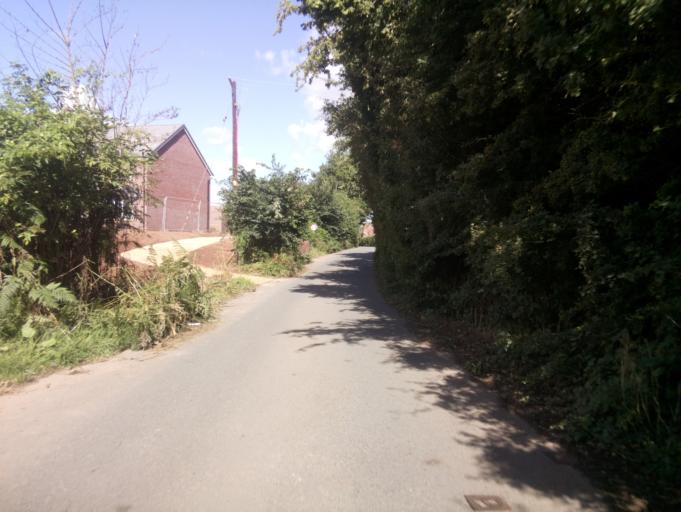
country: GB
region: England
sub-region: Gloucestershire
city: Newent
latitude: 51.9350
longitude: -2.4135
